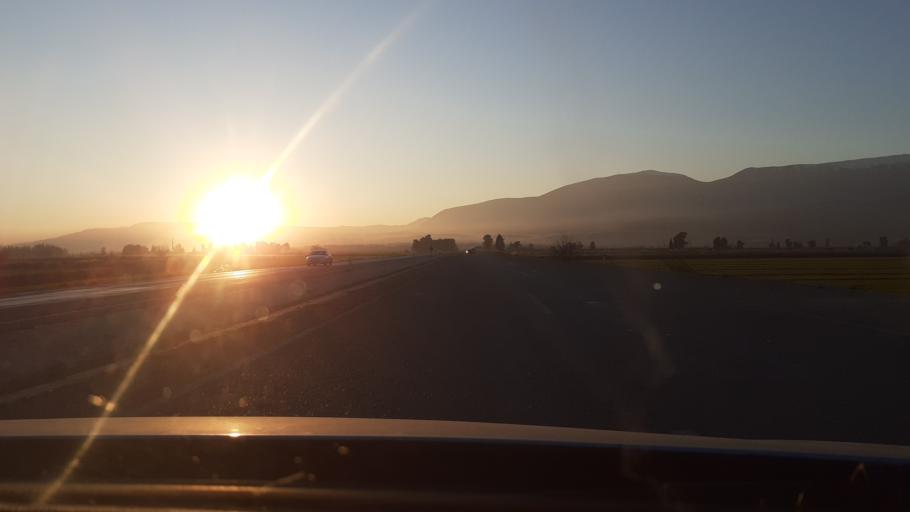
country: TR
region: Hatay
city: Kirikhan
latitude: 36.5068
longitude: 36.4287
